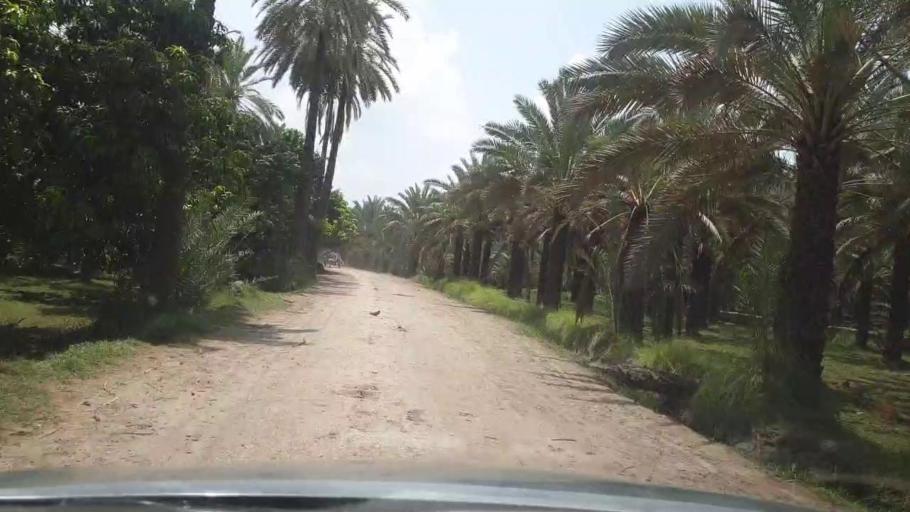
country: PK
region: Sindh
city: Khairpur
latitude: 27.6268
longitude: 68.7426
